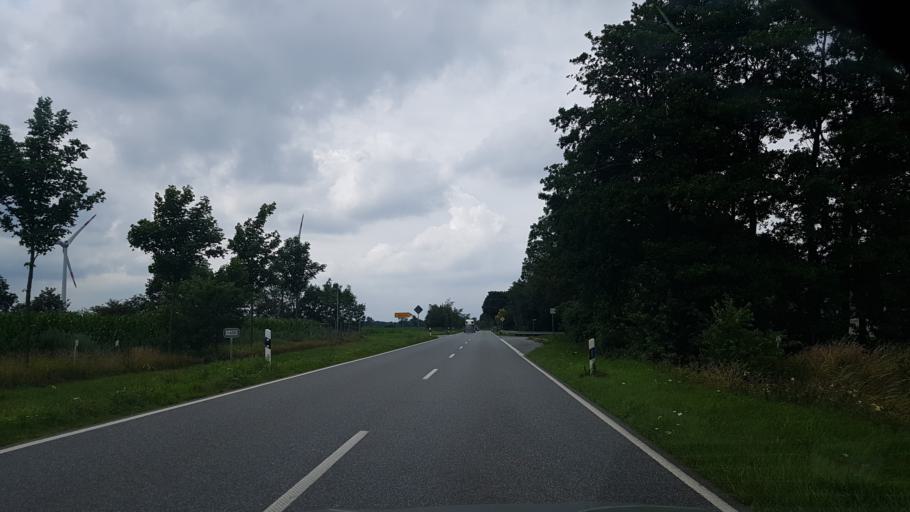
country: DE
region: Schleswig-Holstein
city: Weesby
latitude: 54.8600
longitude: 9.1465
